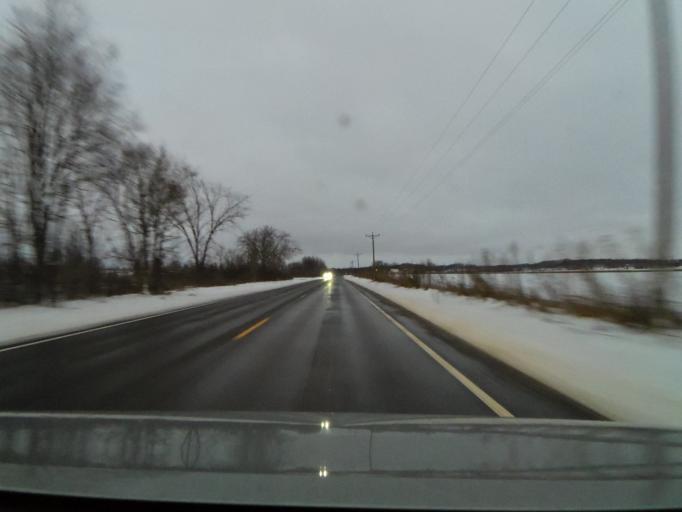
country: US
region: Wisconsin
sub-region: Dunn County
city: Boyceville
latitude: 44.9472
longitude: -92.0435
